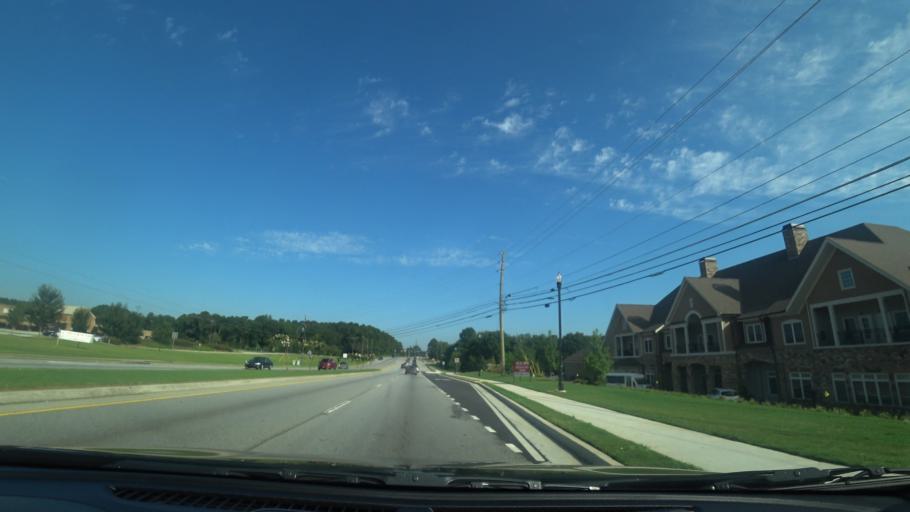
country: US
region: Georgia
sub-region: Gwinnett County
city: Grayson
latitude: 33.9025
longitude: -83.9636
